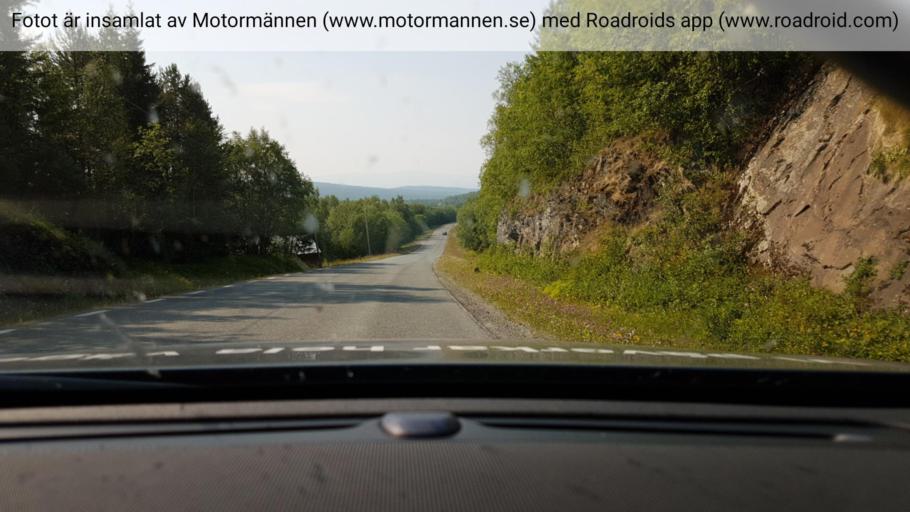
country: NO
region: Nordland
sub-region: Rana
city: Mo i Rana
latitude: 65.7539
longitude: 15.1103
